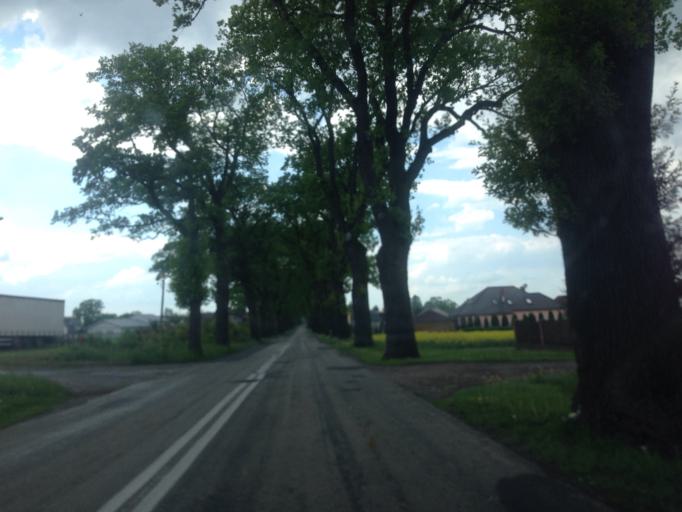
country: PL
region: Kujawsko-Pomorskie
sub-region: Powiat swiecki
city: Pruszcz
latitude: 53.2845
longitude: 18.1336
